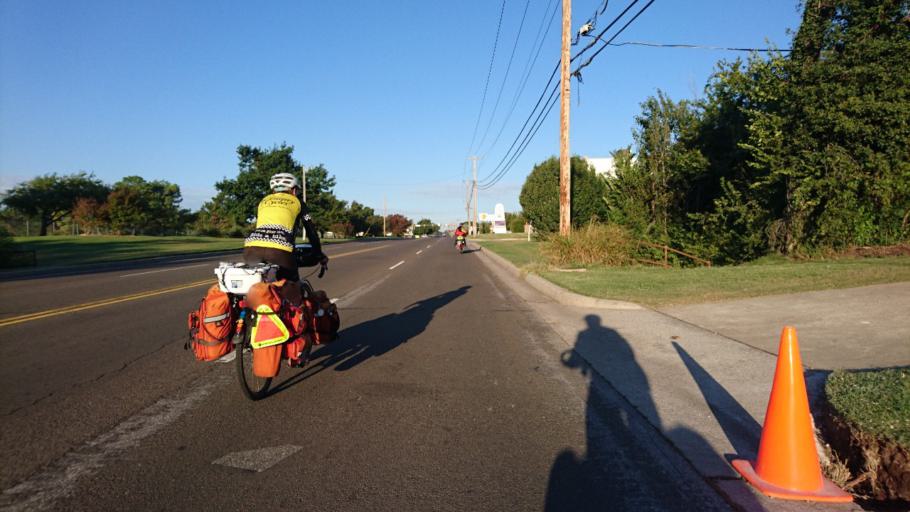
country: US
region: Oklahoma
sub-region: Oklahoma County
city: Warr Acres
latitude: 35.5079
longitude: -97.5805
